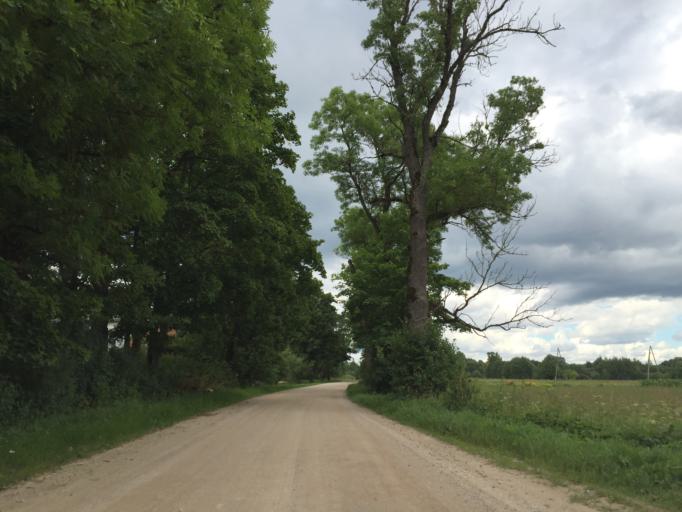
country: LV
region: Malpils
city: Malpils
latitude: 56.9301
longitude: 25.0127
